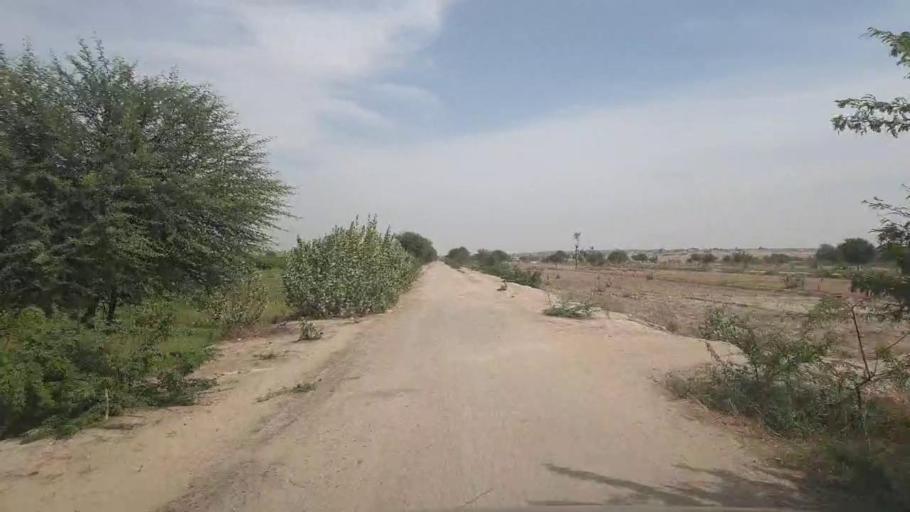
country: PK
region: Sindh
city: Kunri
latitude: 25.2041
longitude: 69.6972
